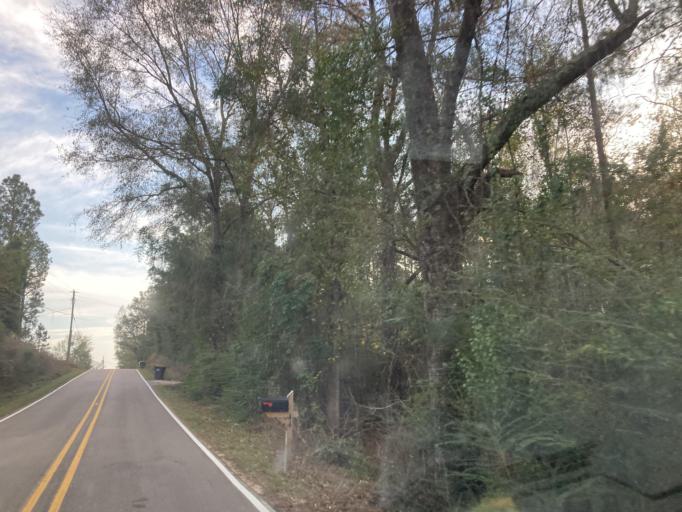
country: US
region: Mississippi
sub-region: Lamar County
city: Purvis
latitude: 31.1897
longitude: -89.3639
